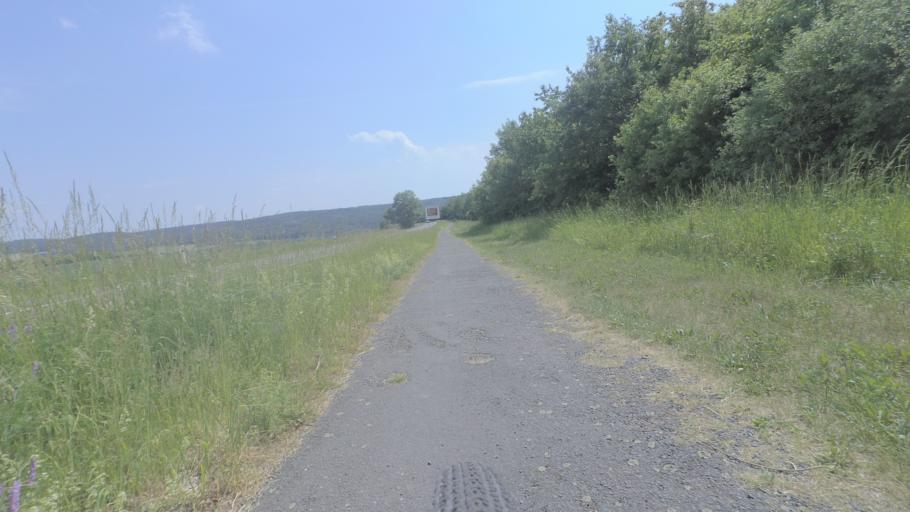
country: DE
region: Saxony-Anhalt
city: Ballenstedt
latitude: 51.7105
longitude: 11.2804
